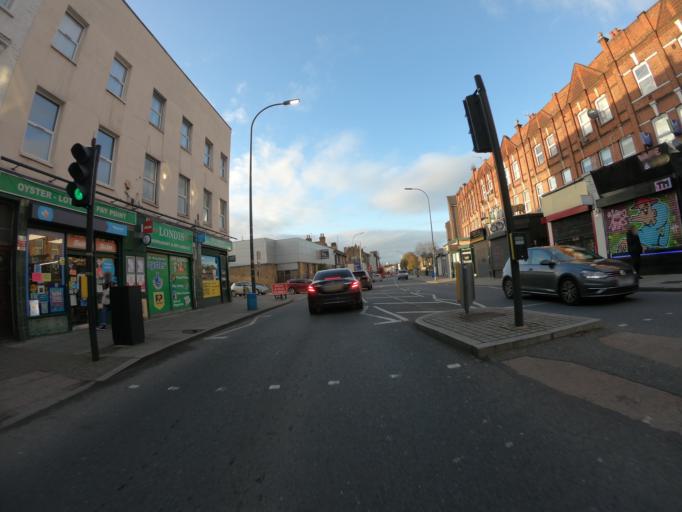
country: GB
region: England
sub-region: Greater London
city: Blackheath
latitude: 51.4590
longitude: -0.0031
